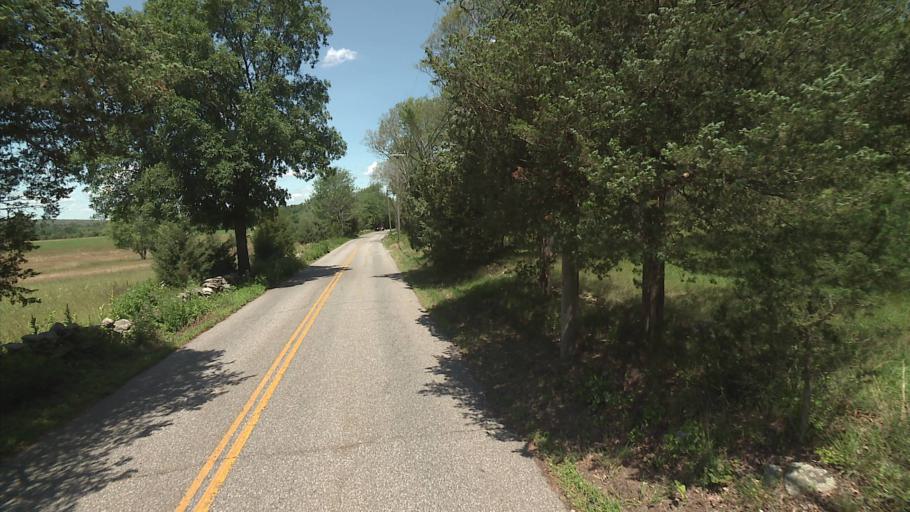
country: US
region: Connecticut
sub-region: New London County
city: Preston City
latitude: 41.5404
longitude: -71.8809
